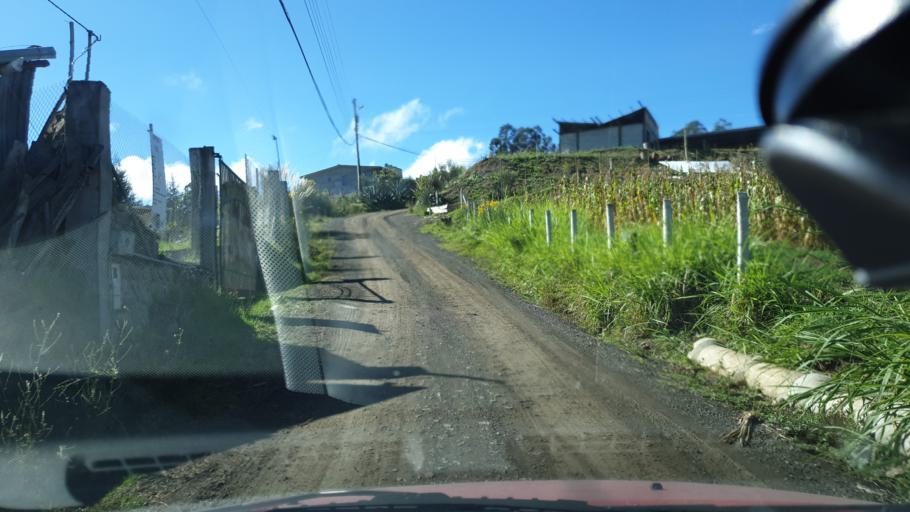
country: EC
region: Azuay
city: Llacao
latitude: -2.8636
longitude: -78.9144
